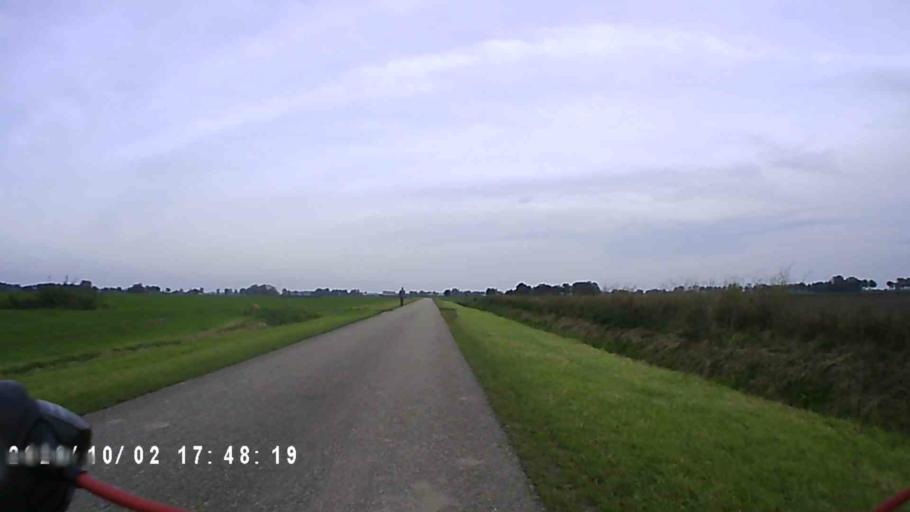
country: NL
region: Groningen
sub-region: Gemeente Zuidhorn
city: Oldehove
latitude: 53.3378
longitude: 6.4001
